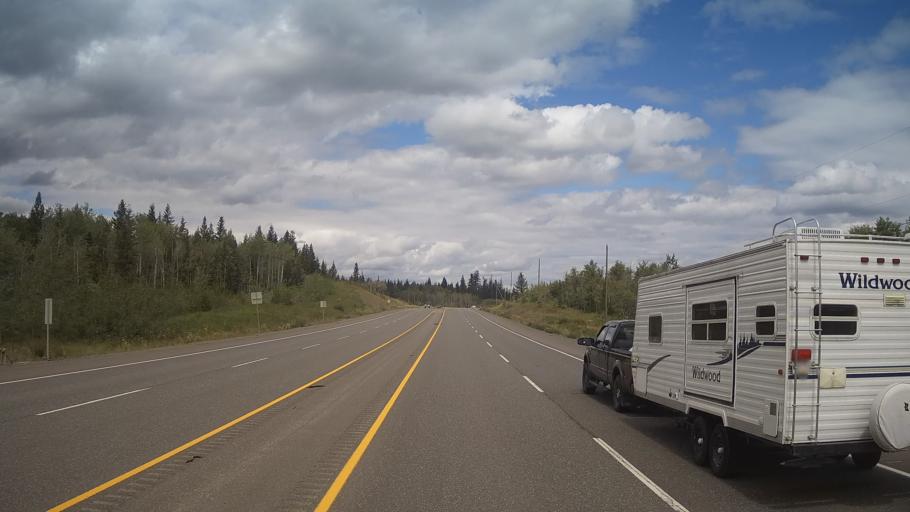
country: CA
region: British Columbia
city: Cache Creek
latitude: 51.3548
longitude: -121.3750
